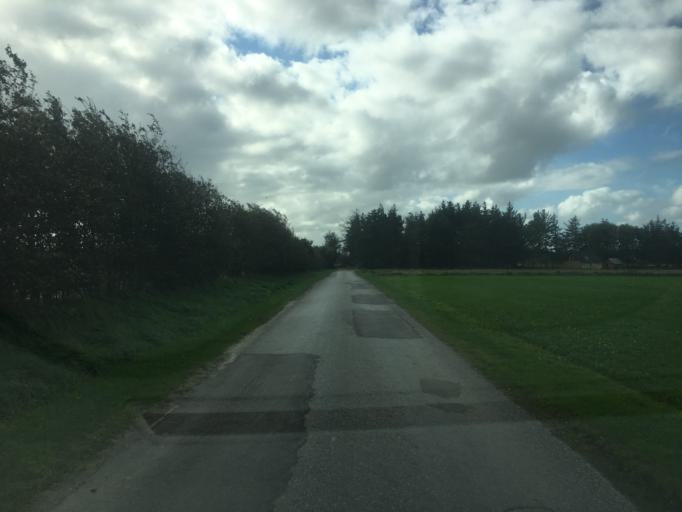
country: DK
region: South Denmark
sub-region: Tonder Kommune
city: Logumkloster
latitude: 55.1091
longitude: 8.8825
